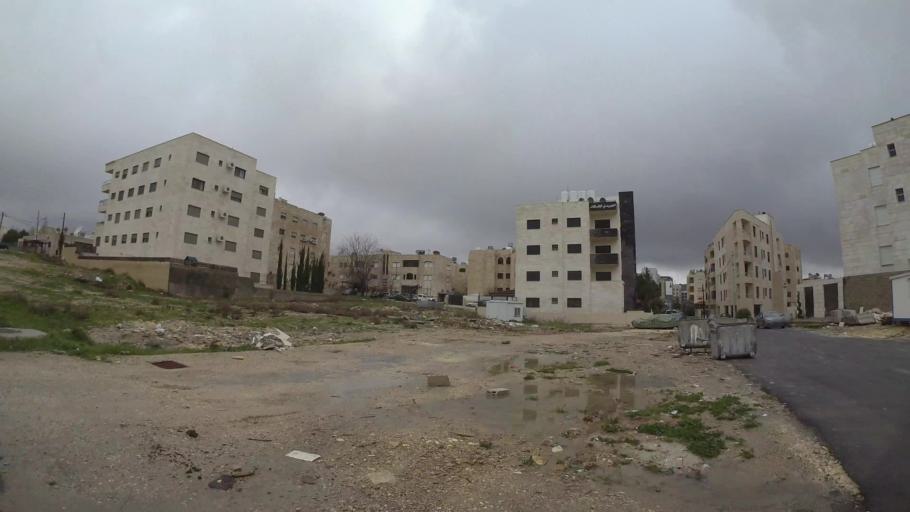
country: JO
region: Amman
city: Wadi as Sir
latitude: 31.9558
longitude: 35.8509
